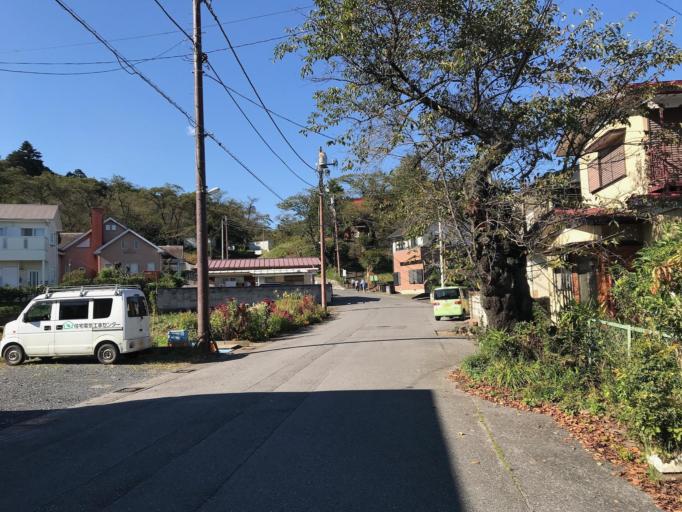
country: JP
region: Tochigi
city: Kanuma
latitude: 36.5714
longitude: 139.7450
